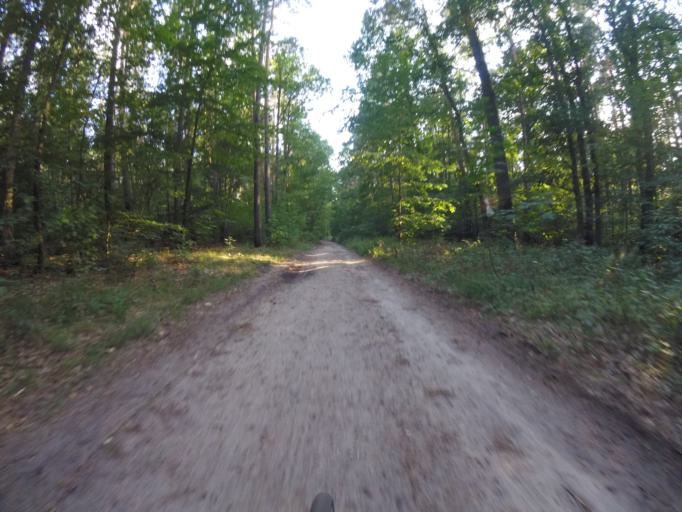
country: DE
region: Brandenburg
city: Petershagen
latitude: 52.5643
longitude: 13.8207
